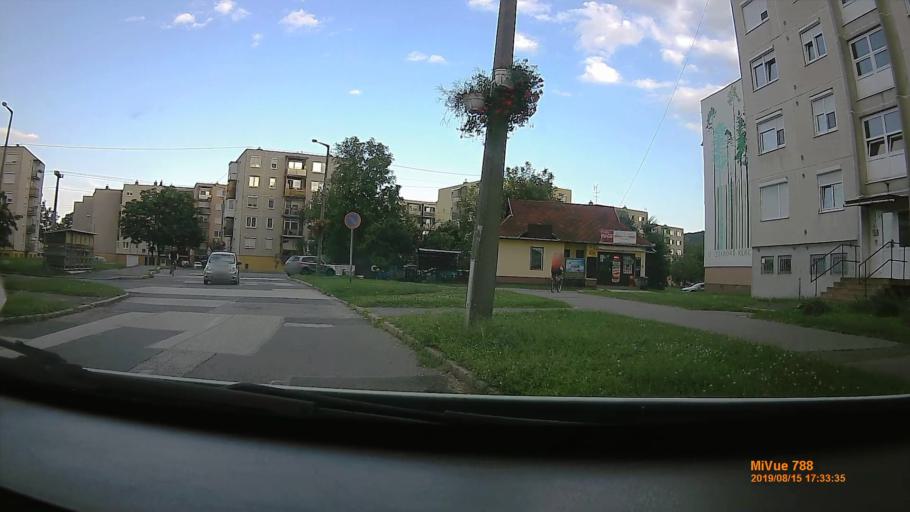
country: HU
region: Borsod-Abauj-Zemplen
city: Kazincbarcika
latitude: 48.2536
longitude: 20.6330
